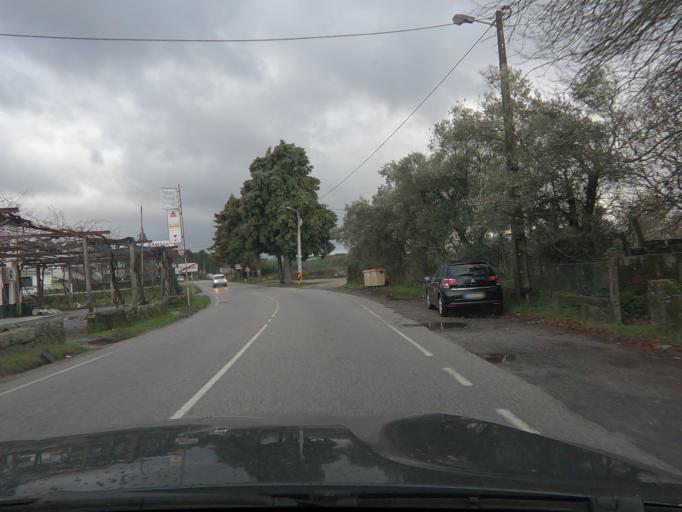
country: PT
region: Vila Real
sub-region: Vila Real
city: Vila Real
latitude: 41.3250
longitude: -7.7288
